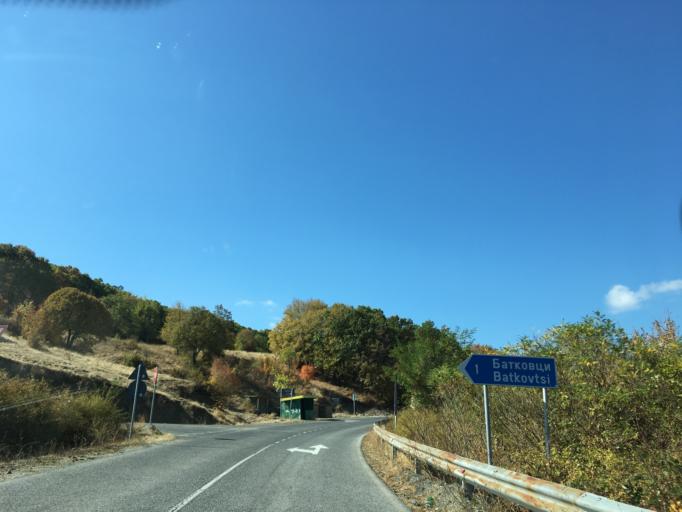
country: BG
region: Kurdzhali
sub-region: Obshtina Krumovgrad
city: Krumovgrad
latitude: 41.4713
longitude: 25.5386
